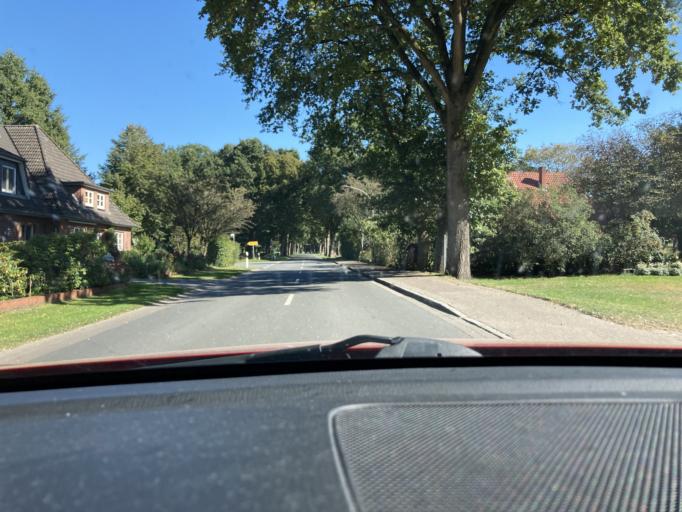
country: DE
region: Lower Saxony
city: Vorwerk
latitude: 53.1538
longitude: 9.1786
